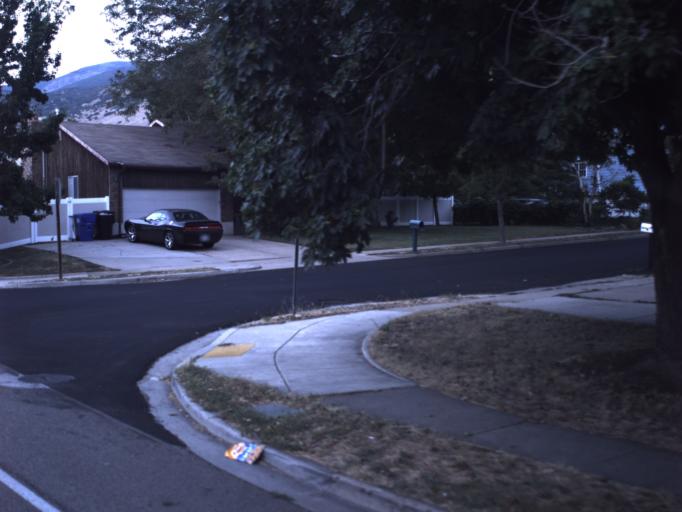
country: US
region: Utah
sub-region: Davis County
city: Centerville
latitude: 40.9304
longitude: -111.8789
